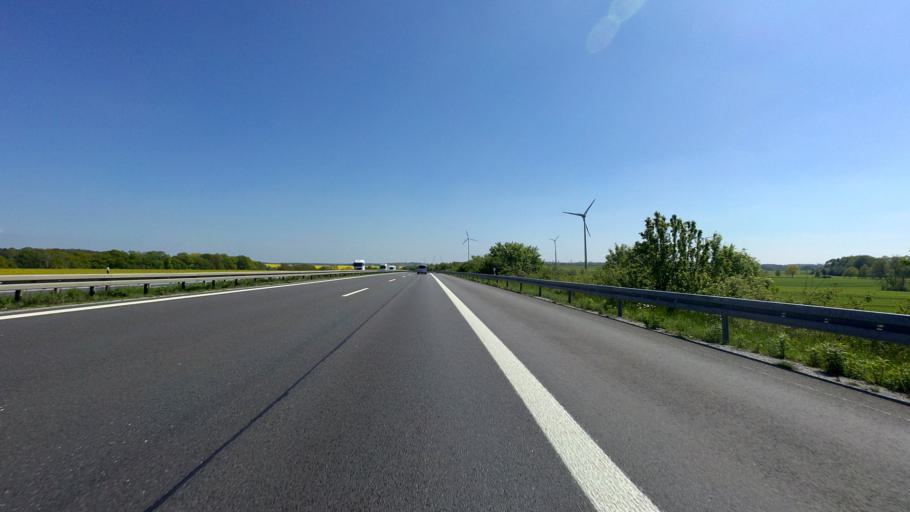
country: DE
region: Saxony
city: Wachau
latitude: 51.1652
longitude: 13.9220
